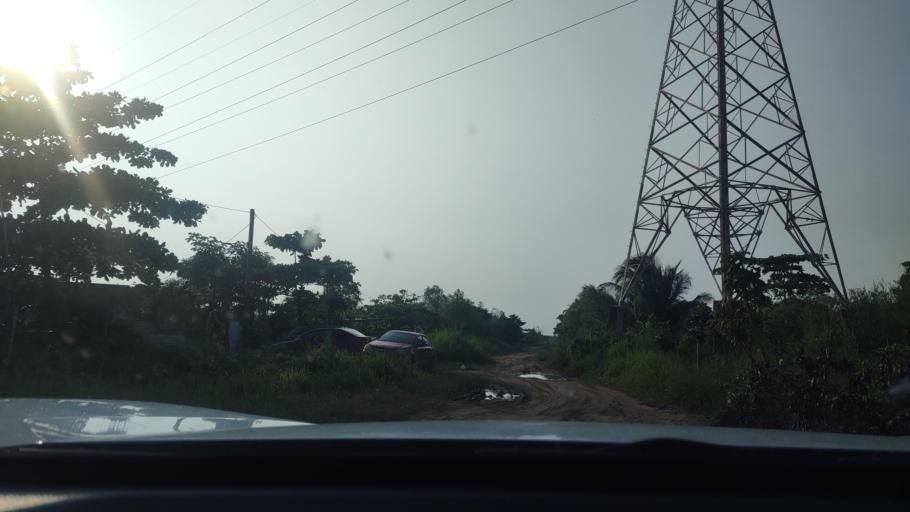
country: MX
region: Veracruz
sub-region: Coatzacoalcos
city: Centro de Readaptacion Social
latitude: 18.1334
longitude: -94.5213
